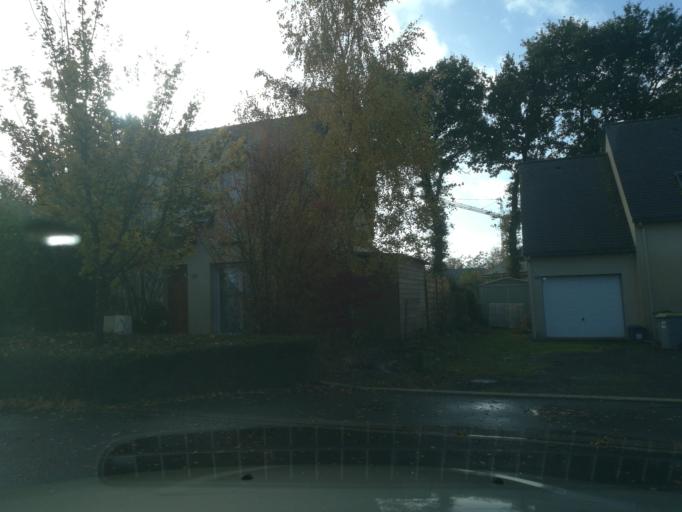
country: FR
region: Brittany
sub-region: Departement d'Ille-et-Vilaine
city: Pleumeleuc
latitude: 48.1819
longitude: -1.9267
